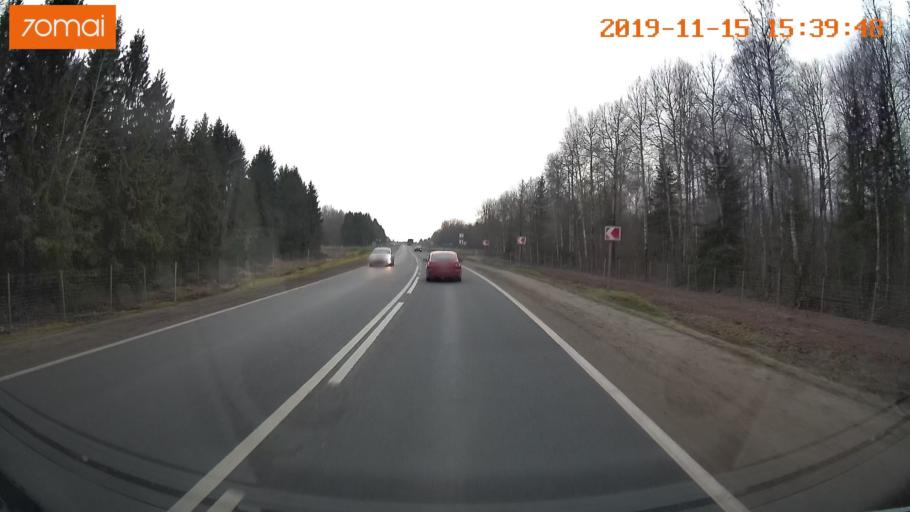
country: RU
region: Jaroslavl
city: Danilov
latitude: 58.0181
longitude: 40.0636
